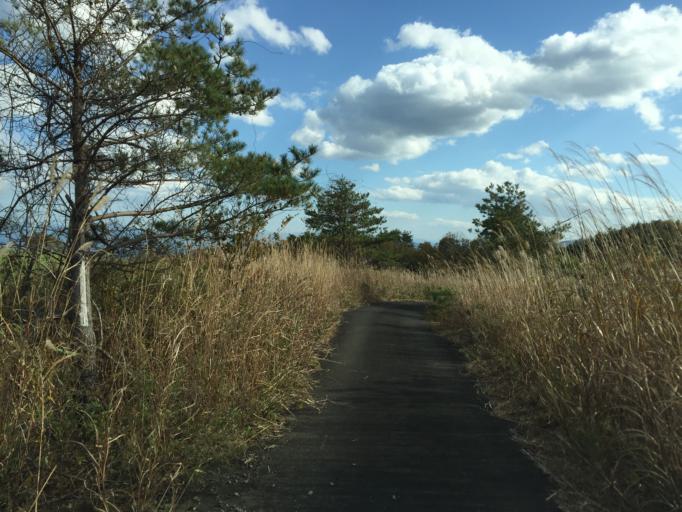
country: JP
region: Fukushima
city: Fukushima-shi
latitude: 37.7344
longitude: 140.3186
